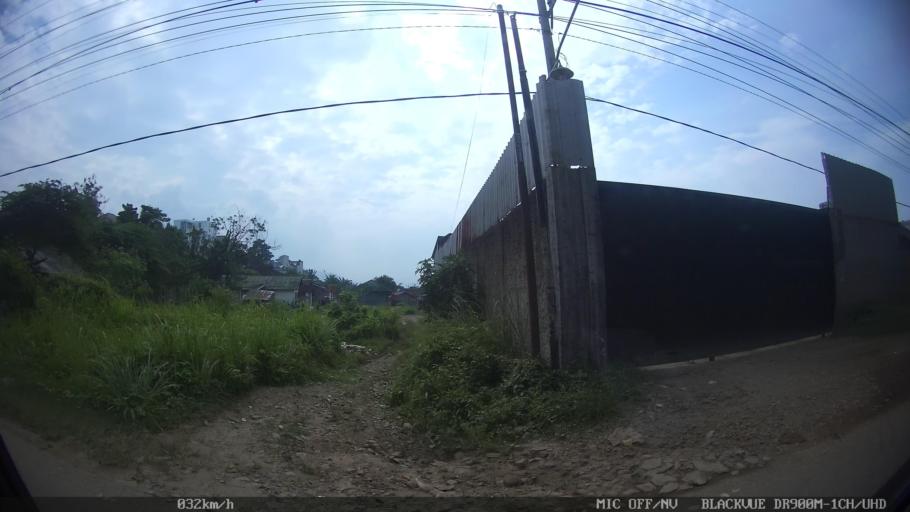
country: ID
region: Lampung
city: Bandarlampung
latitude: -5.4522
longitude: 105.2434
